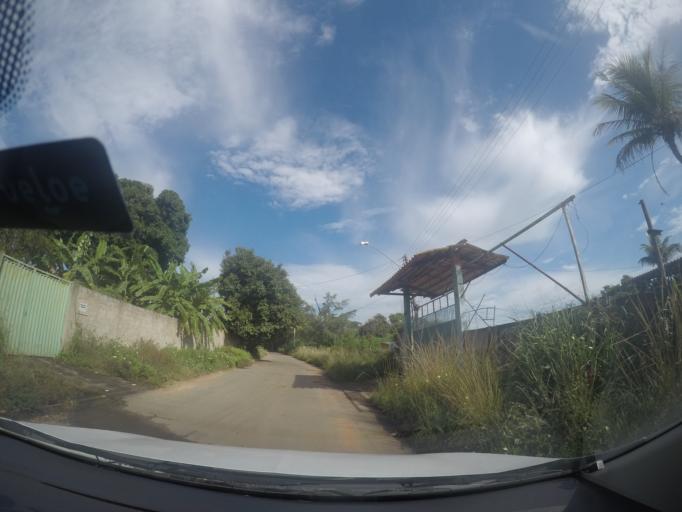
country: BR
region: Goias
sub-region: Goiania
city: Goiania
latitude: -16.6712
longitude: -49.1989
